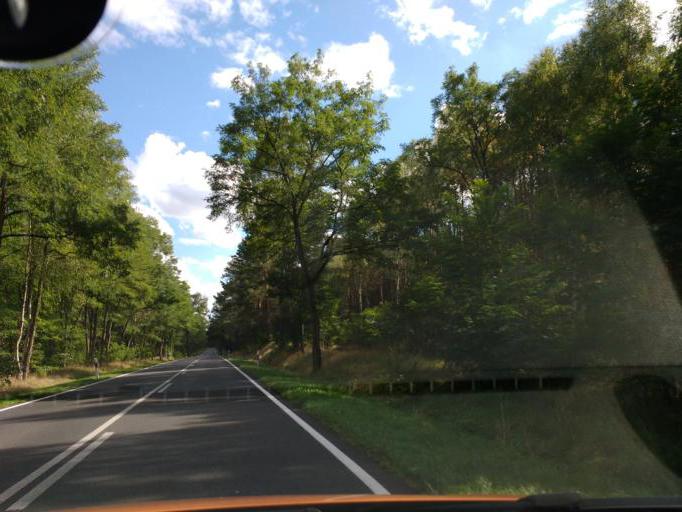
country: DE
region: Brandenburg
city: Wendisch Rietz
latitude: 52.2148
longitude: 13.9881
